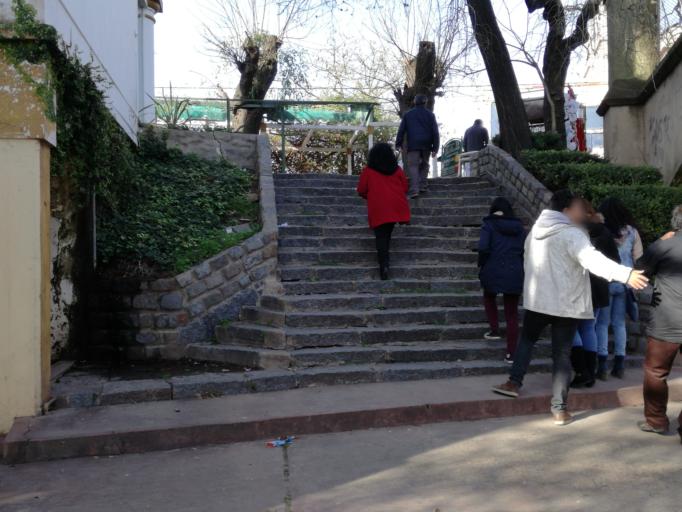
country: AR
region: Buenos Aires
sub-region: Partido de Lujan
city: Lujan
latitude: -34.5633
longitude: -59.1231
